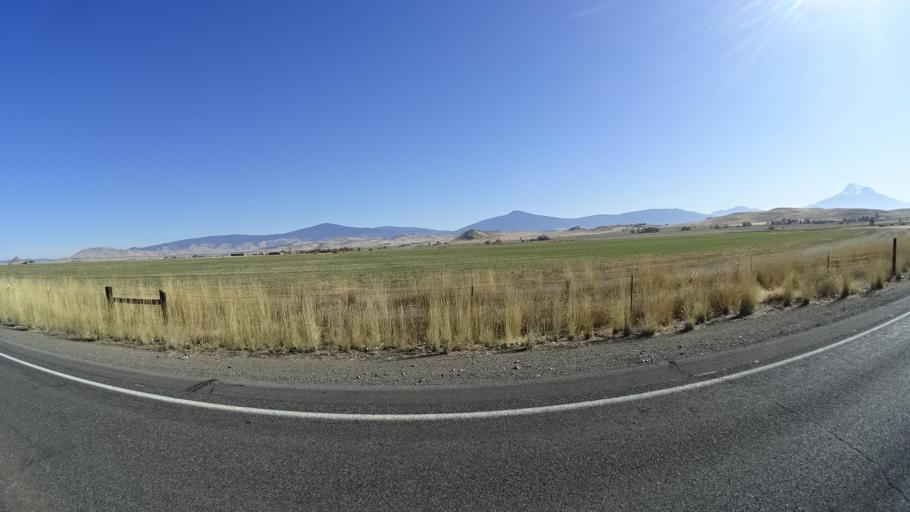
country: US
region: California
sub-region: Siskiyou County
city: Montague
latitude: 41.7518
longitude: -122.5247
